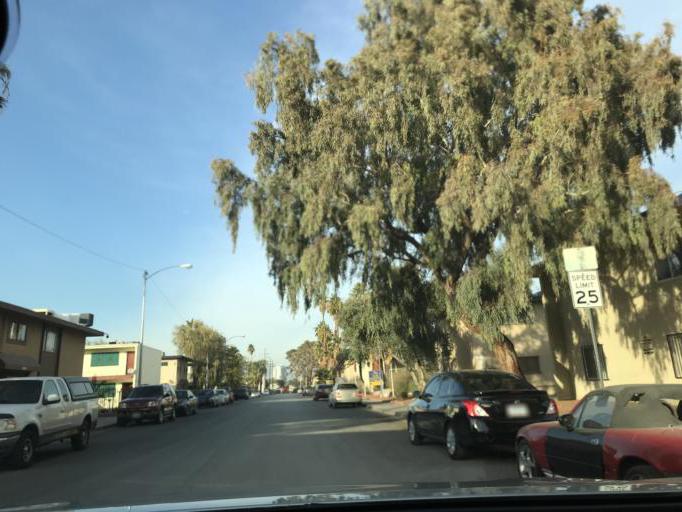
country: US
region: Nevada
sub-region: Clark County
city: Winchester
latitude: 36.1406
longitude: -115.1483
